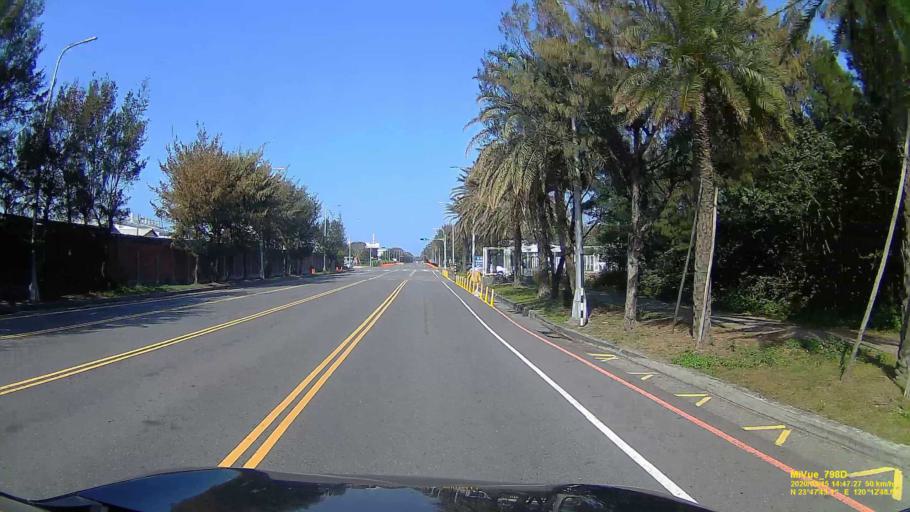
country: TW
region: Taiwan
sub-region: Yunlin
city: Douliu
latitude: 23.7954
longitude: 120.2135
